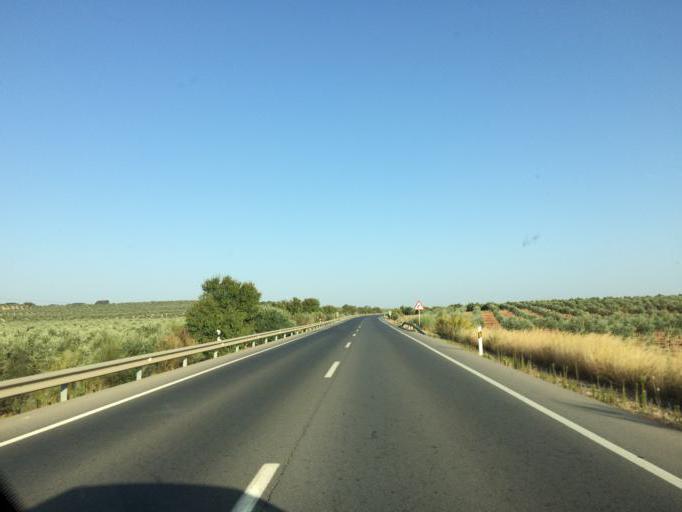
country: ES
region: Andalusia
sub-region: Provincia de Malaga
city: Humilladero
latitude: 37.0530
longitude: -4.6636
